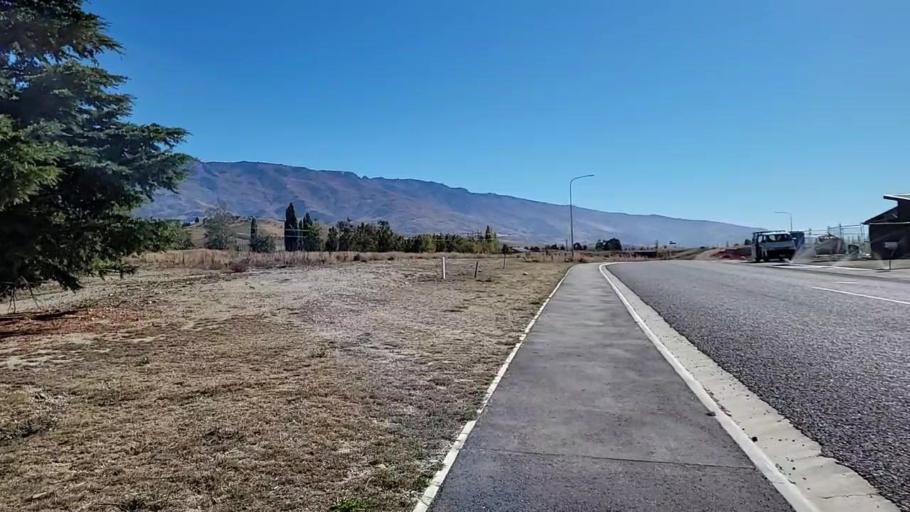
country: NZ
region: Otago
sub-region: Queenstown-Lakes District
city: Wanaka
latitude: -44.9774
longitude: 169.2373
